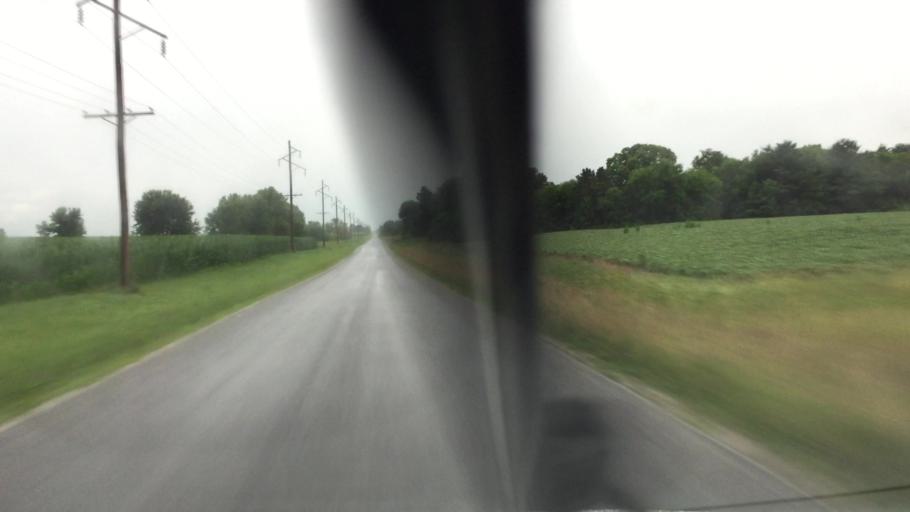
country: US
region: Illinois
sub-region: Hancock County
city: Hamilton
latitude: 40.4460
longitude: -91.2711
